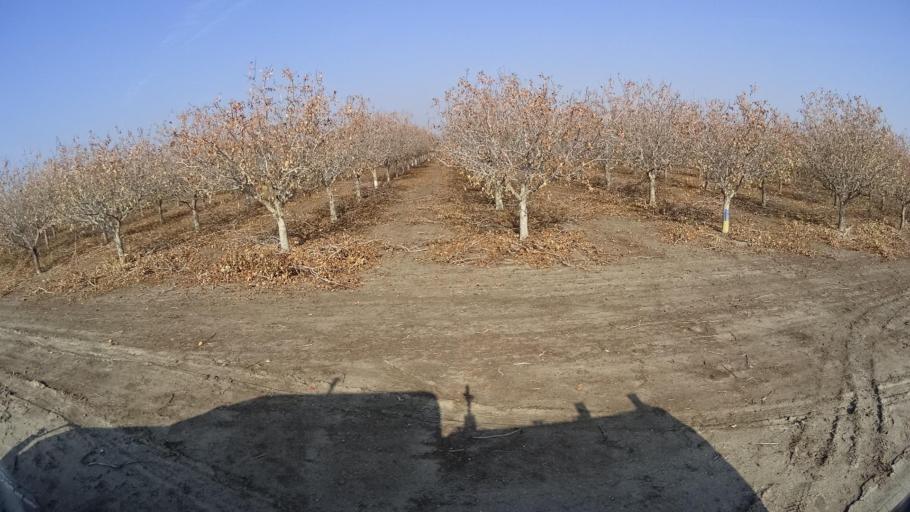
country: US
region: California
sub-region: Kern County
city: Buttonwillow
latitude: 35.3404
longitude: -119.3785
